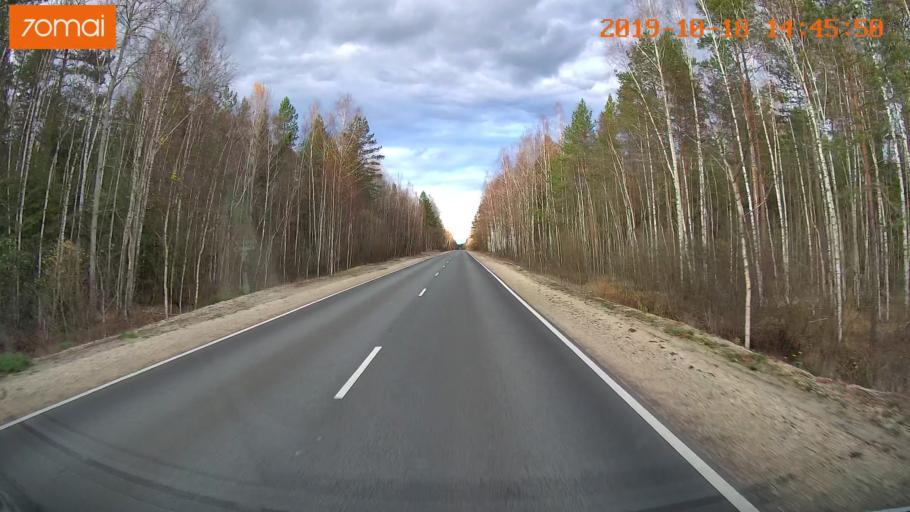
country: RU
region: Vladimir
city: Velikodvorskiy
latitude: 55.3613
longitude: 40.6797
